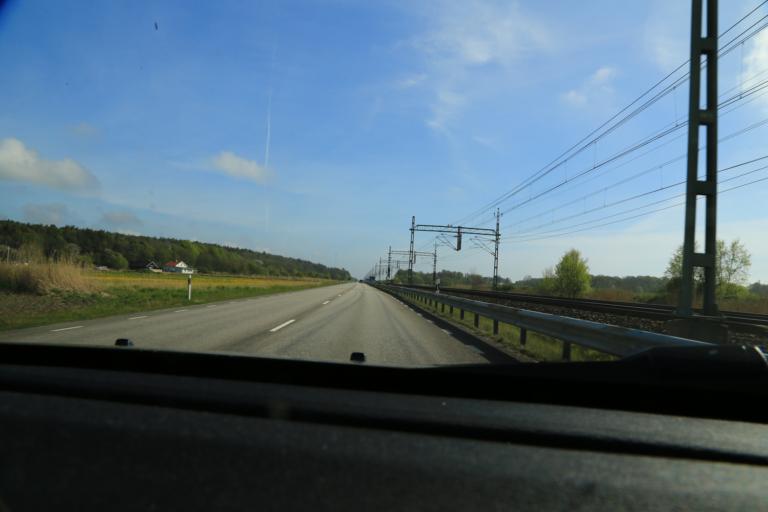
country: SE
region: Halland
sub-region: Varbergs Kommun
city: Varberg
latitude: 57.1994
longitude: 12.2226
